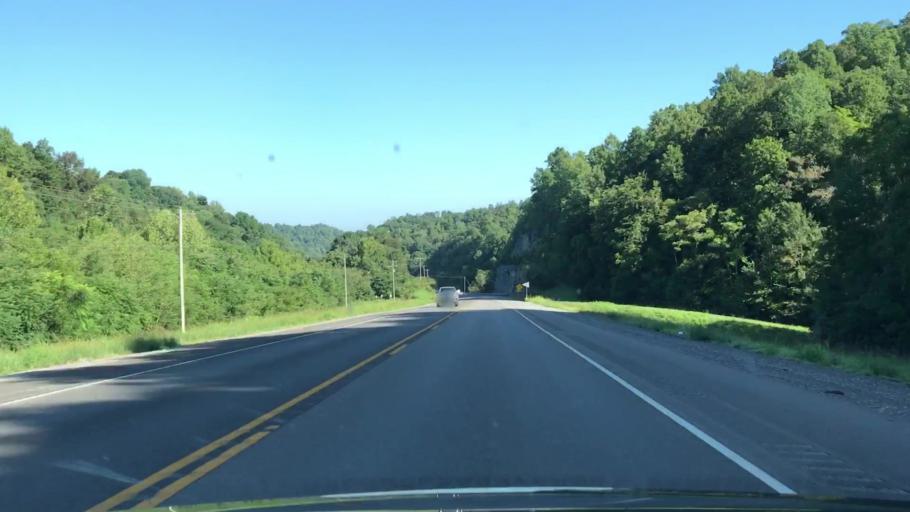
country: US
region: Kentucky
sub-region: Cumberland County
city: Burkesville
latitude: 36.7180
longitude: -85.3653
